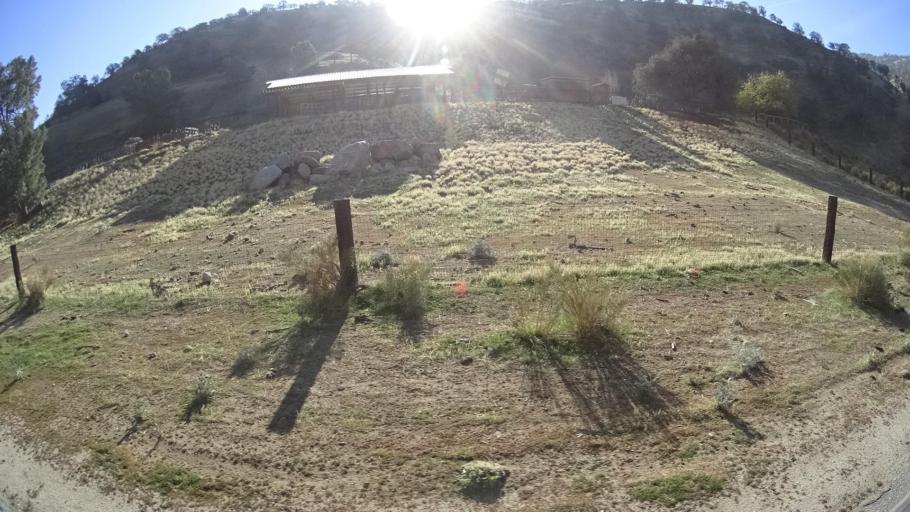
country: US
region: California
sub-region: Kern County
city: Bear Valley Springs
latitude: 35.3142
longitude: -118.5547
